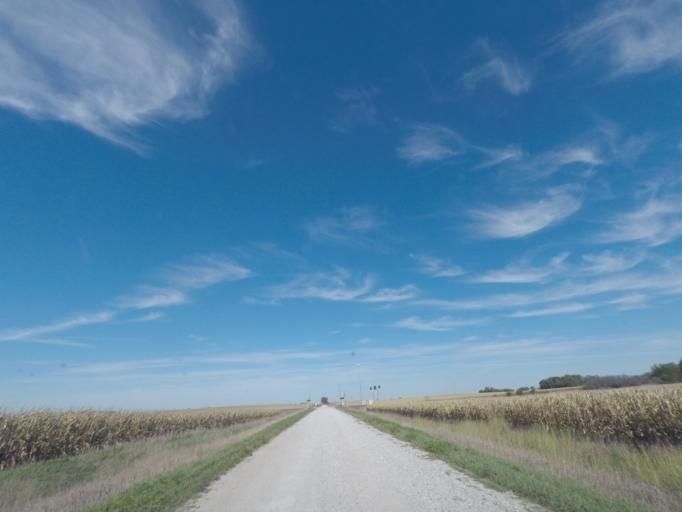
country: US
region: Iowa
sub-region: Story County
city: Nevada
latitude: 42.0179
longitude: -93.3573
